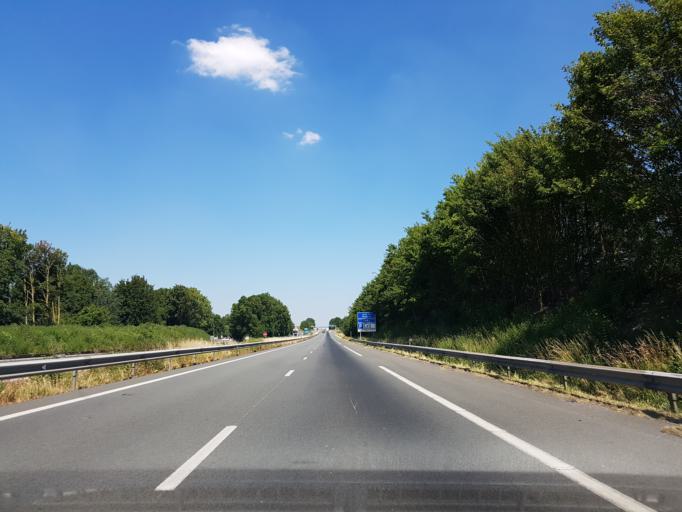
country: FR
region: Nord-Pas-de-Calais
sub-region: Departement du Nord
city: Marcoing
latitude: 50.0827
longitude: 3.1734
